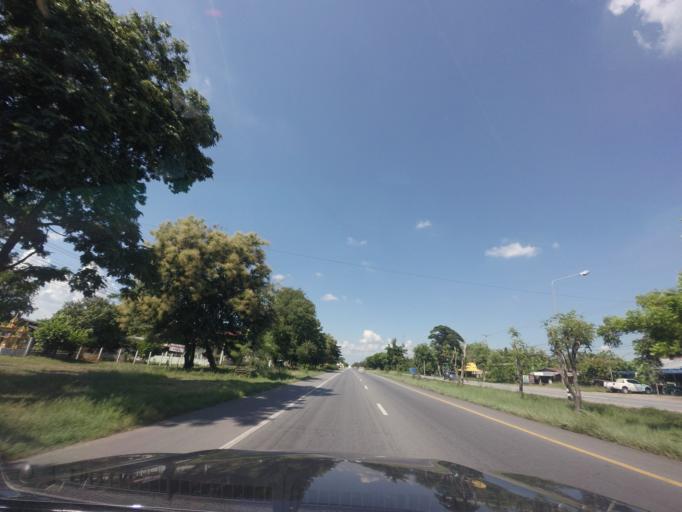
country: TH
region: Nakhon Ratchasima
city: Non Sung
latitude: 15.1499
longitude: 102.3260
